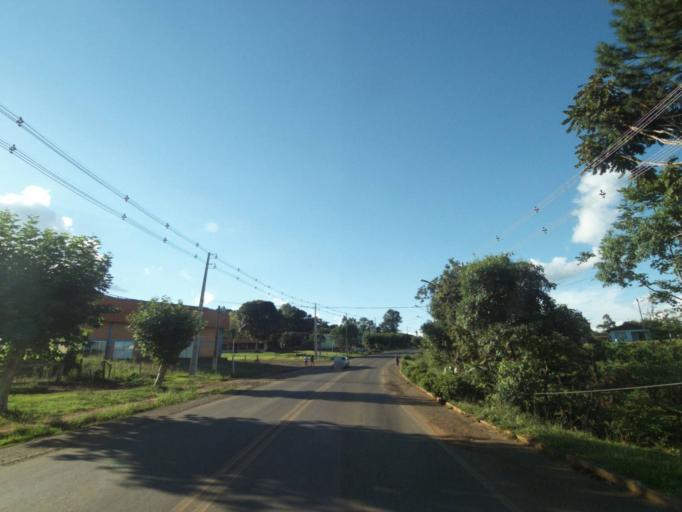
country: BR
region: Parana
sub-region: Uniao Da Vitoria
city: Uniao da Vitoria
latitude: -26.1660
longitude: -51.5353
